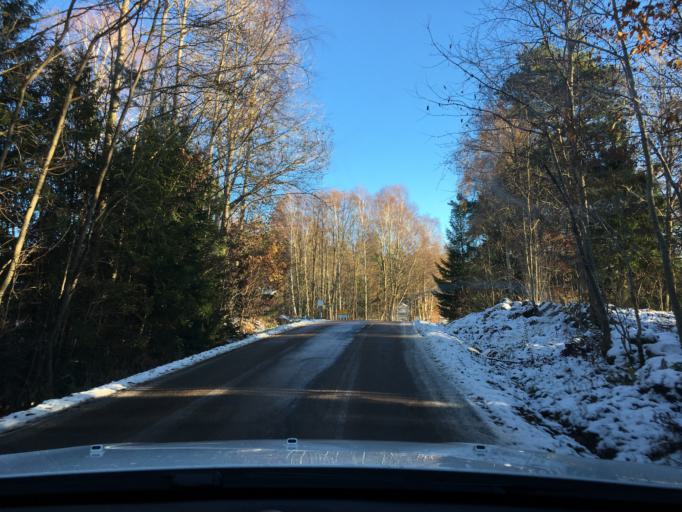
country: SE
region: Vaestra Goetaland
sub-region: Tjorns Kommun
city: Myggenas
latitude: 58.0941
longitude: 11.7441
